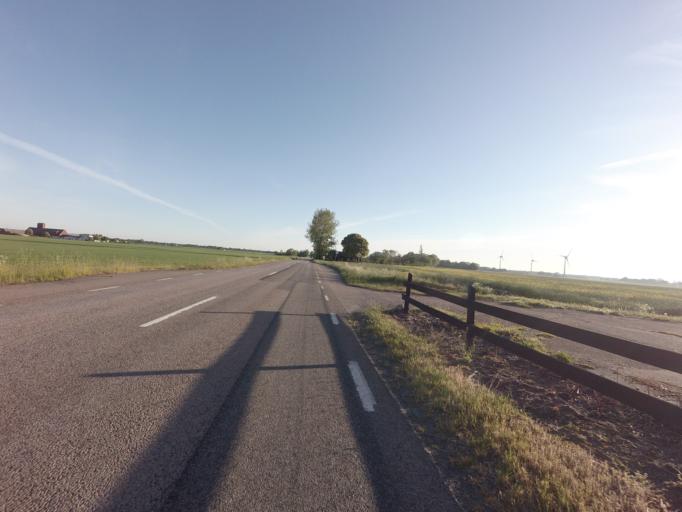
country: SE
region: Skane
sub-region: Helsingborg
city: Odakra
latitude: 56.1923
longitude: 12.6754
